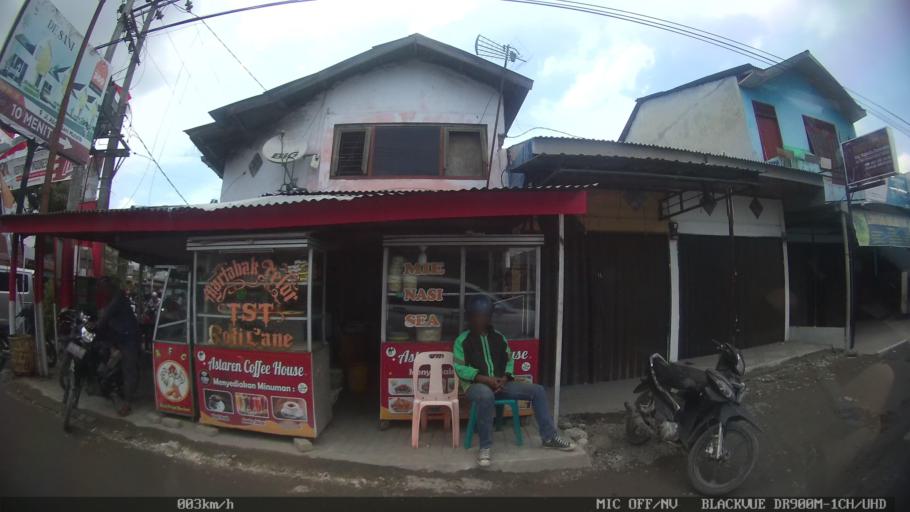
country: ID
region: North Sumatra
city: Labuhan Deli
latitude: 3.6971
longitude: 98.6564
